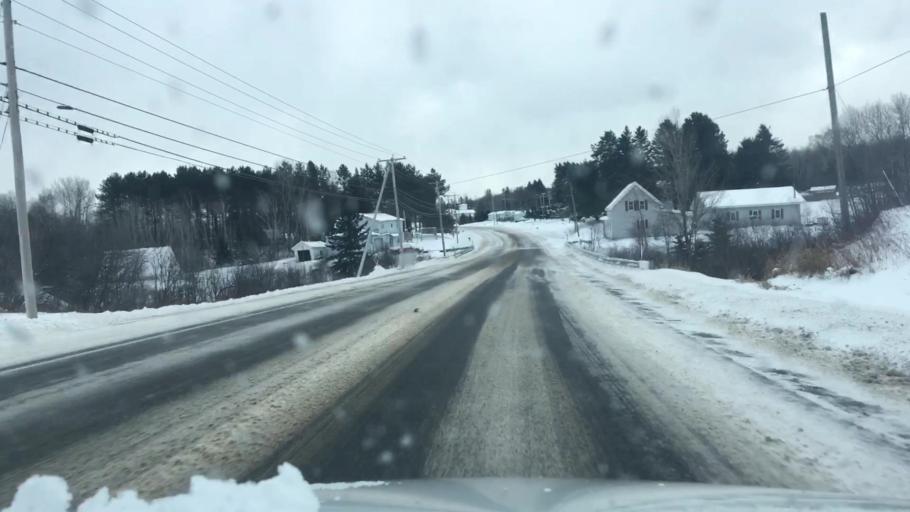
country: US
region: Maine
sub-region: Aroostook County
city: Madawaska
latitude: 47.3149
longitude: -68.1613
